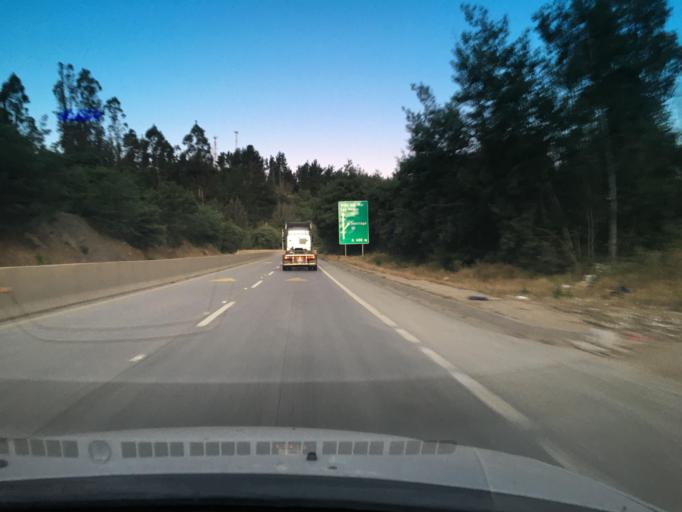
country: CL
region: Valparaiso
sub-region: Provincia de Valparaiso
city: Vina del Mar
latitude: -33.1065
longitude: -71.5625
